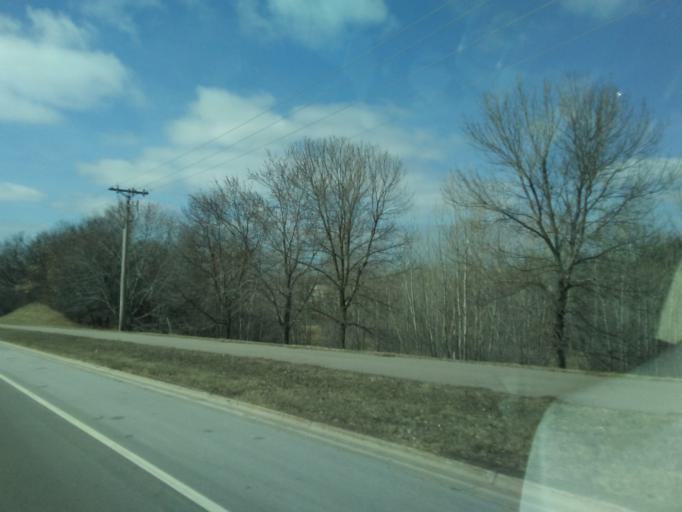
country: US
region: Minnesota
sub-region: Dakota County
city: Eagan
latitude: 44.8336
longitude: -93.1269
